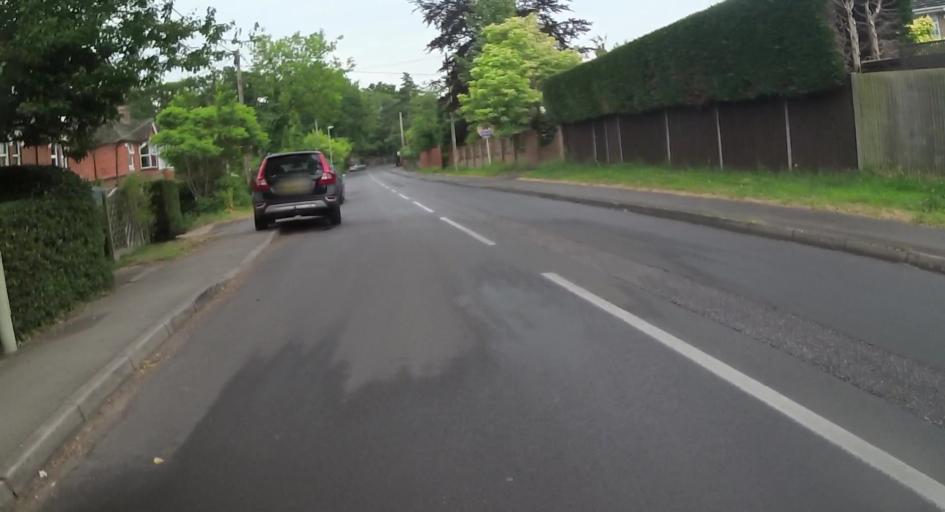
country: GB
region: England
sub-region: Hampshire
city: Fleet
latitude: 51.2632
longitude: -0.8505
